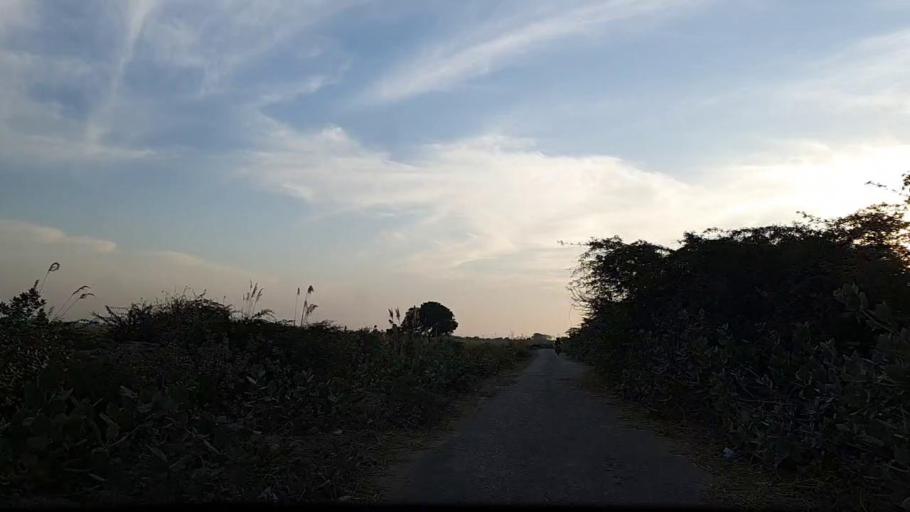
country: PK
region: Sindh
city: Mirpur Batoro
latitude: 24.6409
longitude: 68.1407
